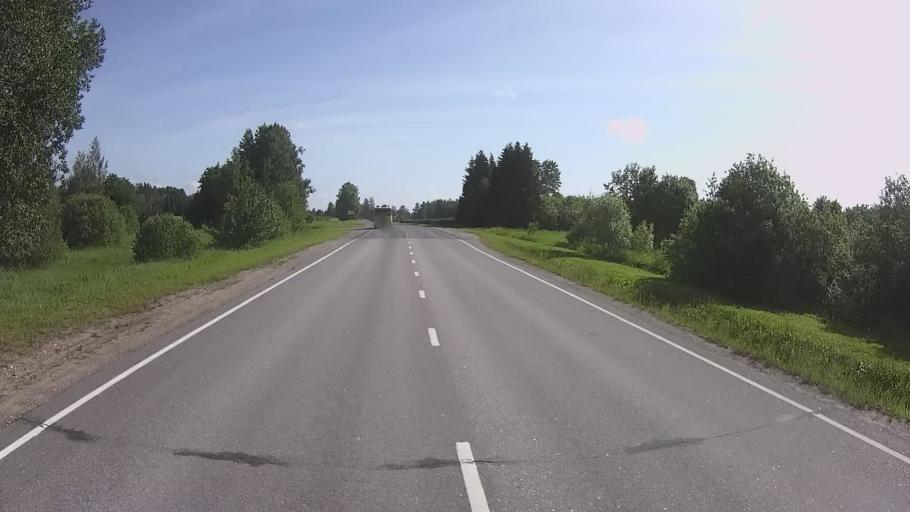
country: EE
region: Valgamaa
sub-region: Torva linn
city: Torva
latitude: 58.0104
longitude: 25.9385
